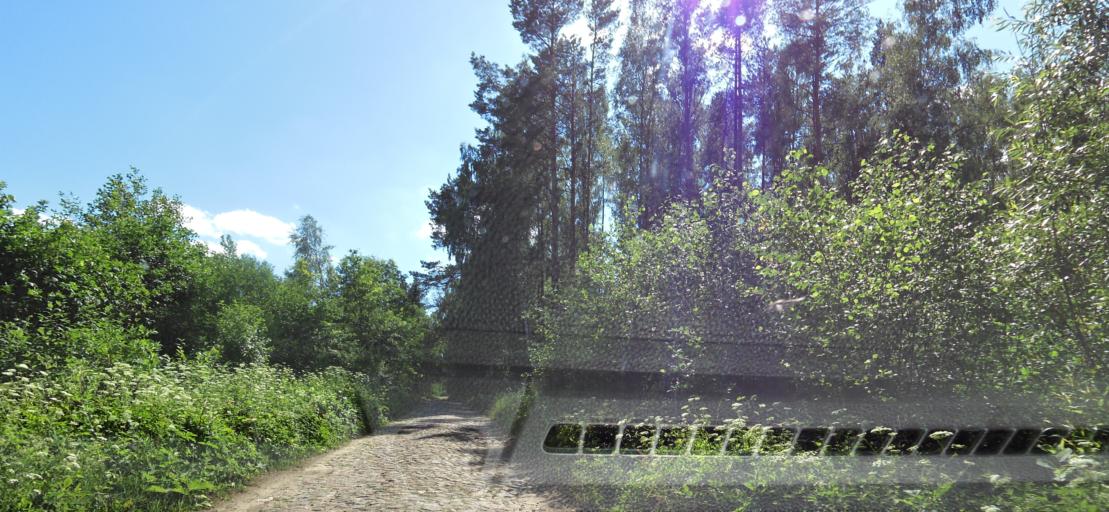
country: LT
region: Vilnius County
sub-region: Vilnius
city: Fabijoniskes
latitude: 54.8394
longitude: 25.3267
